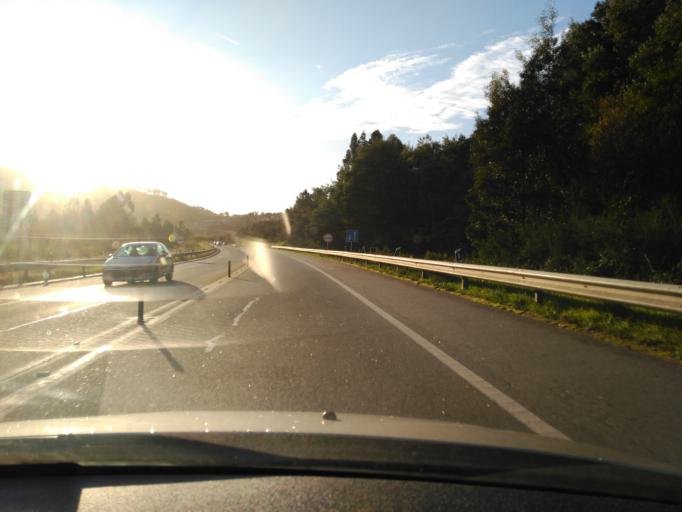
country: PT
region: Braga
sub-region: Guimaraes
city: Guimaraes
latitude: 41.4515
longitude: -8.2607
